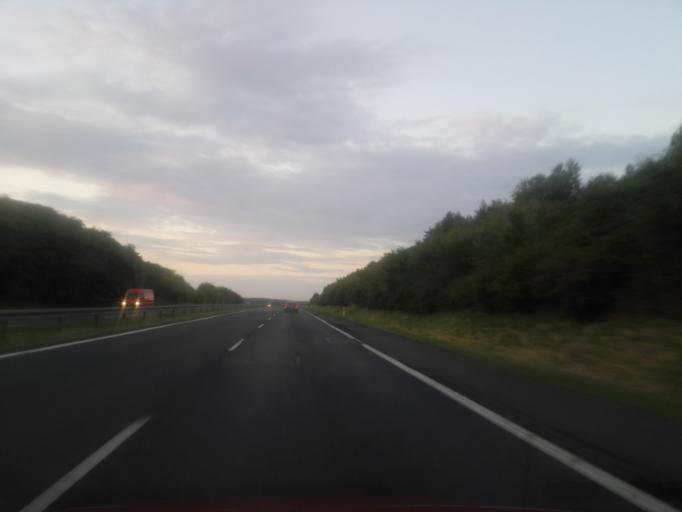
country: PL
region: Lodz Voivodeship
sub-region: Powiat radomszczanski
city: Gomunice
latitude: 51.1403
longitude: 19.4250
